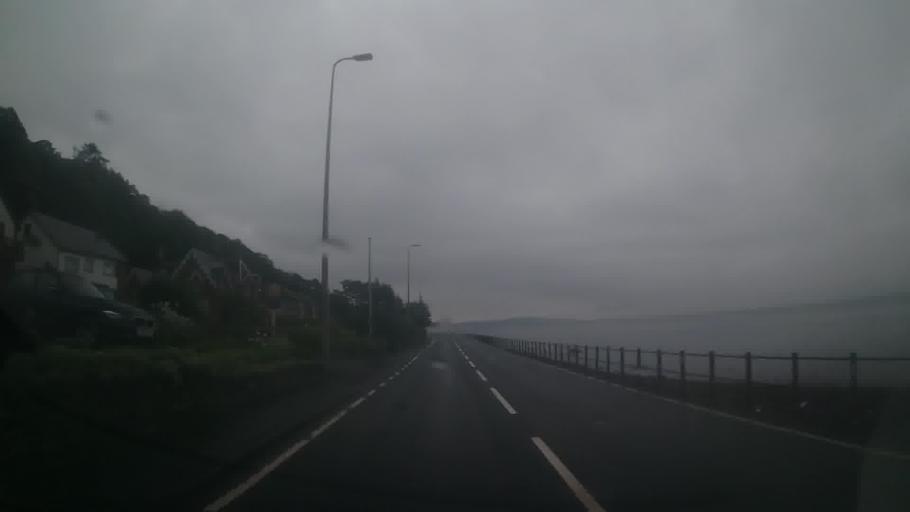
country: GB
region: Scotland
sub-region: North Ayrshire
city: Skelmorlie
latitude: 55.8645
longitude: -4.8913
